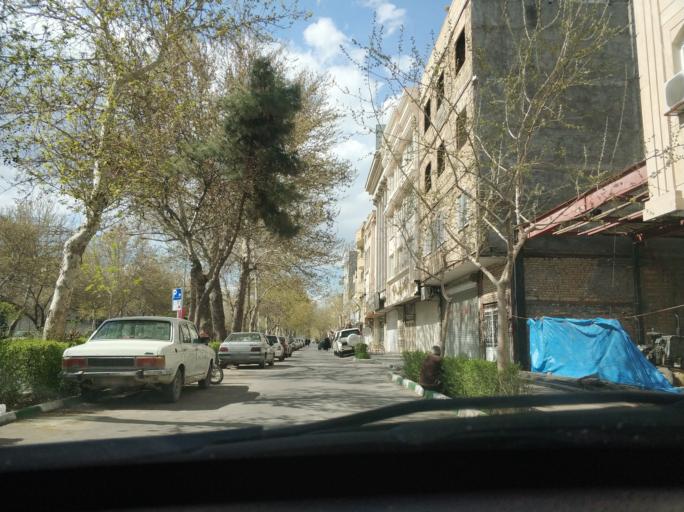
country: IR
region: Razavi Khorasan
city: Mashhad
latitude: 36.2698
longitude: 59.5972
